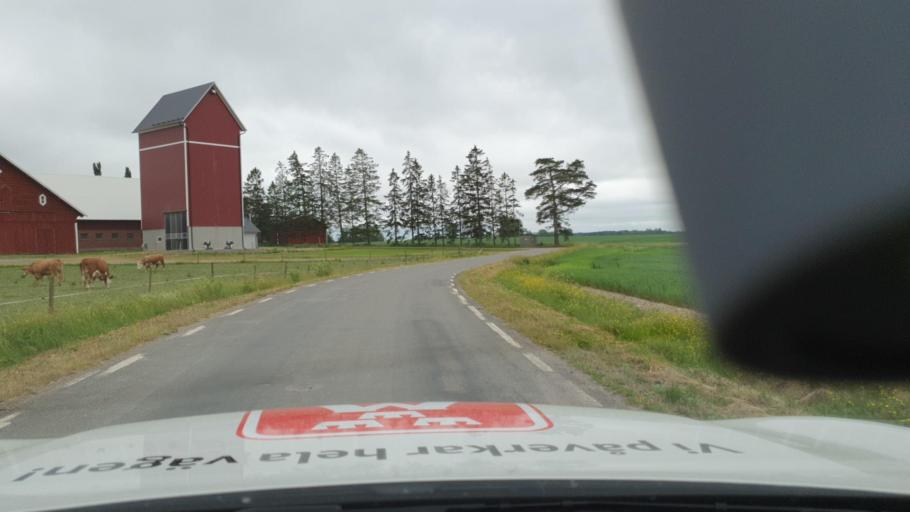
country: SE
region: Vaestra Goetaland
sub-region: Tibro Kommun
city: Tibro
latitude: 58.3745
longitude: 14.1152
